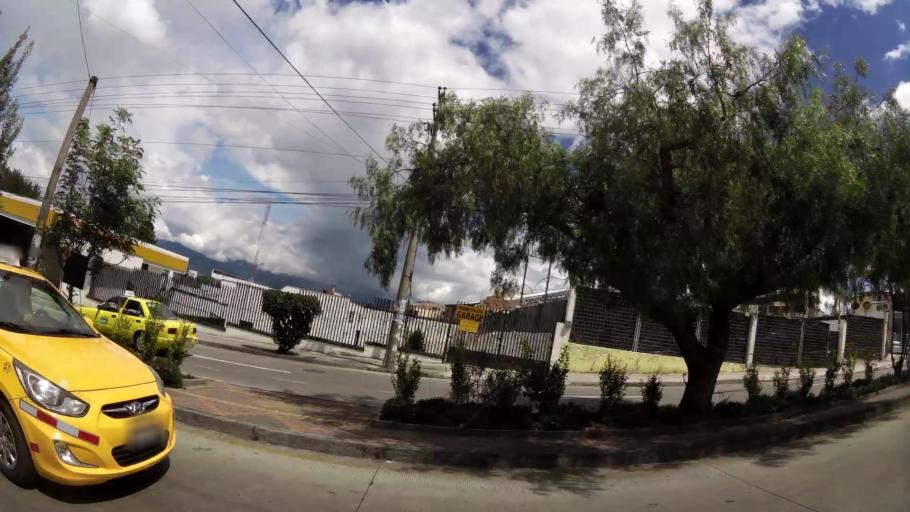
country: EC
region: Tungurahua
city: Ambato
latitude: -1.2367
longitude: -78.6190
